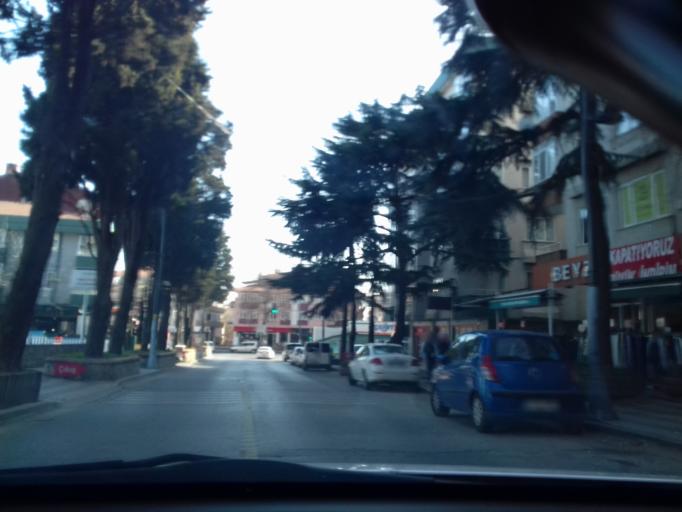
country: TR
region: Istanbul
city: Umraniye
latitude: 41.0200
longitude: 29.0816
